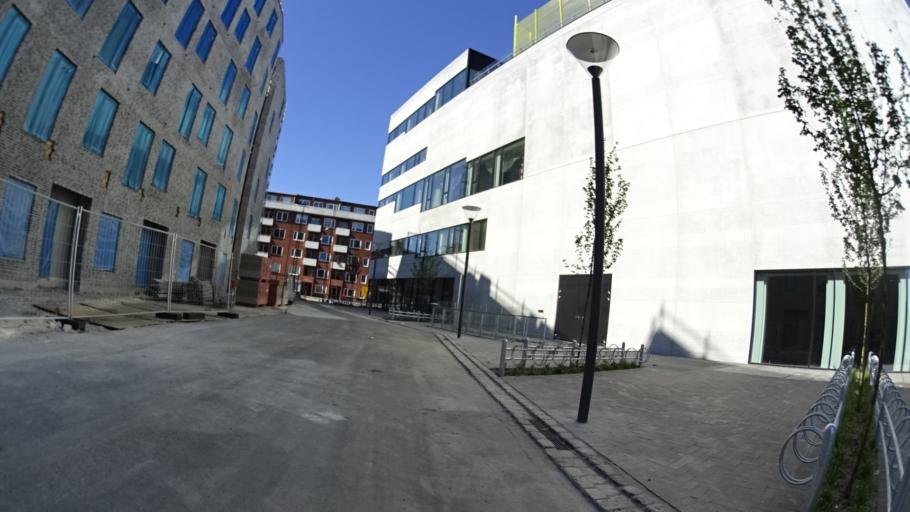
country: DK
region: Central Jutland
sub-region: Arhus Kommune
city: Arhus
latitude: 56.1563
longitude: 10.1899
